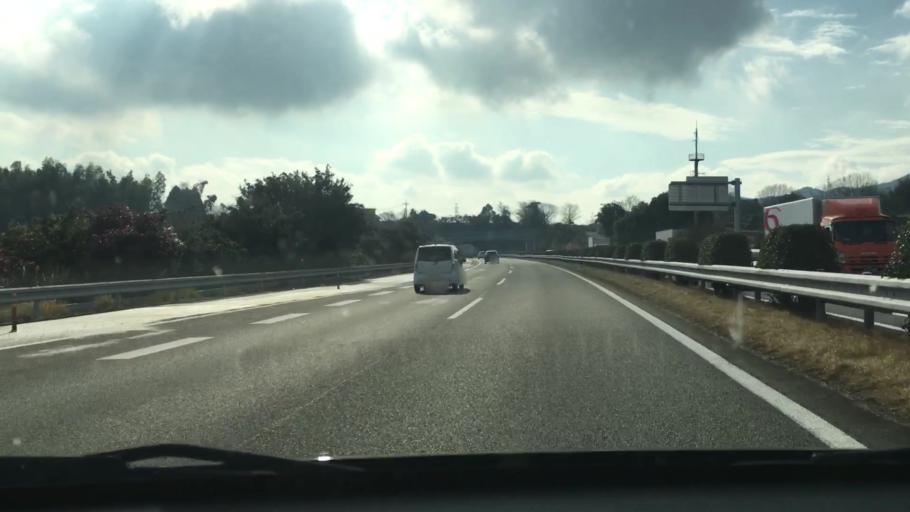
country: JP
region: Kumamoto
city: Uto
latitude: 32.6929
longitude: 130.7401
